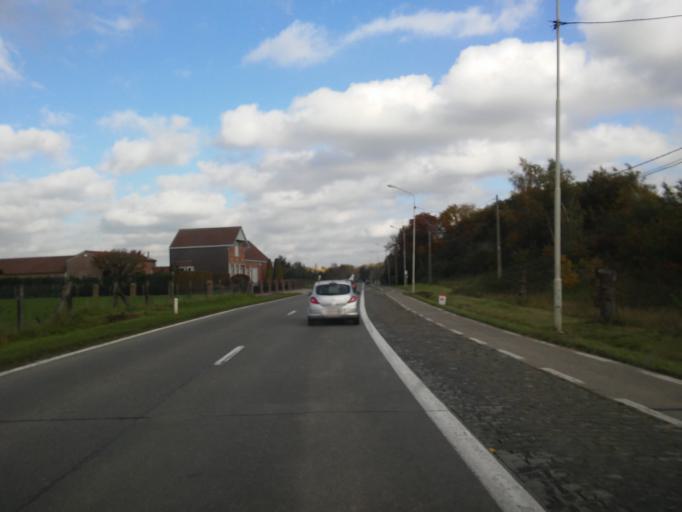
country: BE
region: Flanders
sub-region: Provincie Antwerpen
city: Duffel
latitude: 51.1101
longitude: 4.5264
